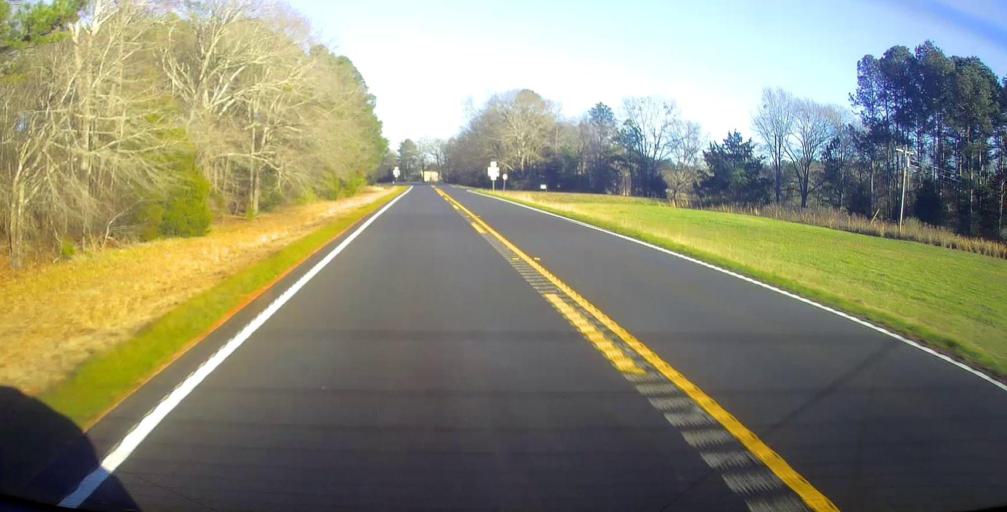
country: US
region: Georgia
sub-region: Meriwether County
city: Greenville
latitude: 32.9120
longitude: -84.7401
